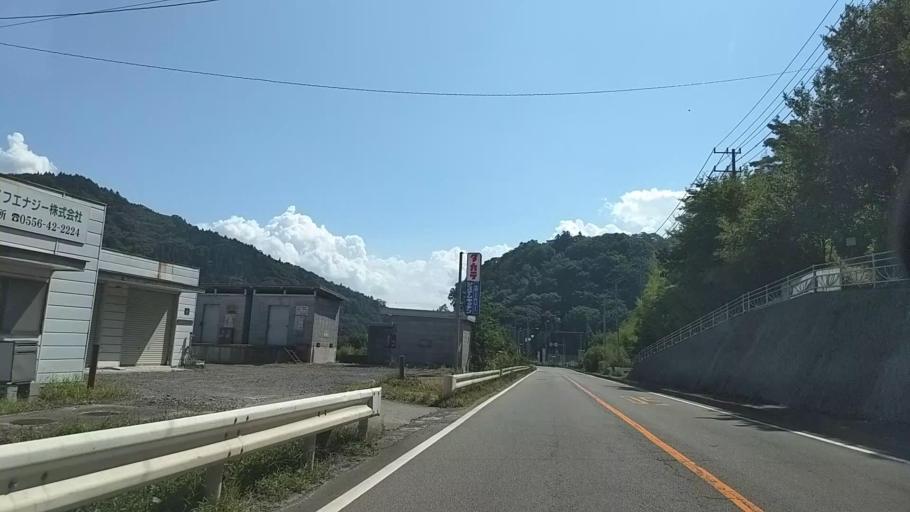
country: JP
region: Yamanashi
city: Ryuo
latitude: 35.4744
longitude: 138.4441
